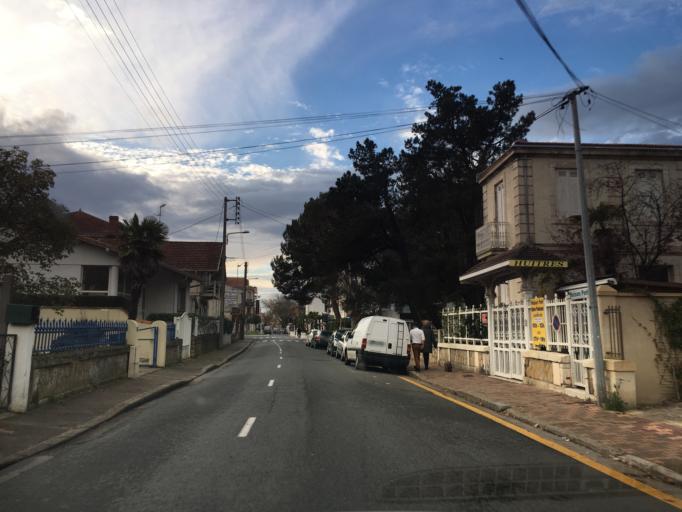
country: FR
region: Aquitaine
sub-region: Departement de la Gironde
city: Arcachon
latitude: 44.6628
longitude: -1.1627
